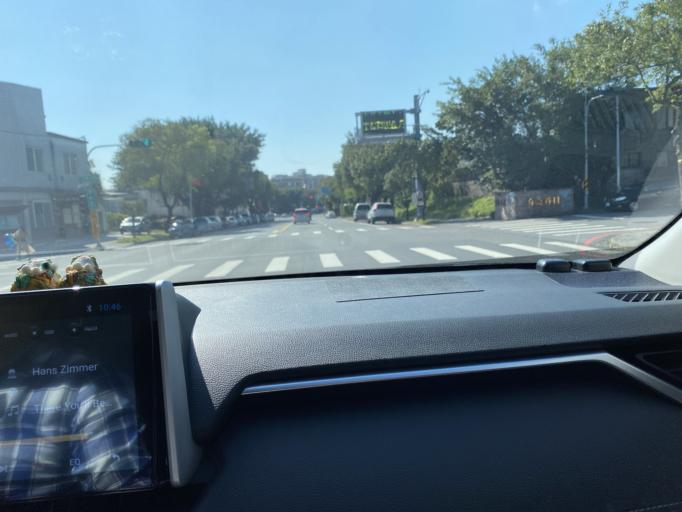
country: TW
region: Taiwan
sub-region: Hualien
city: Hualian
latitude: 23.9876
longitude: 121.6211
